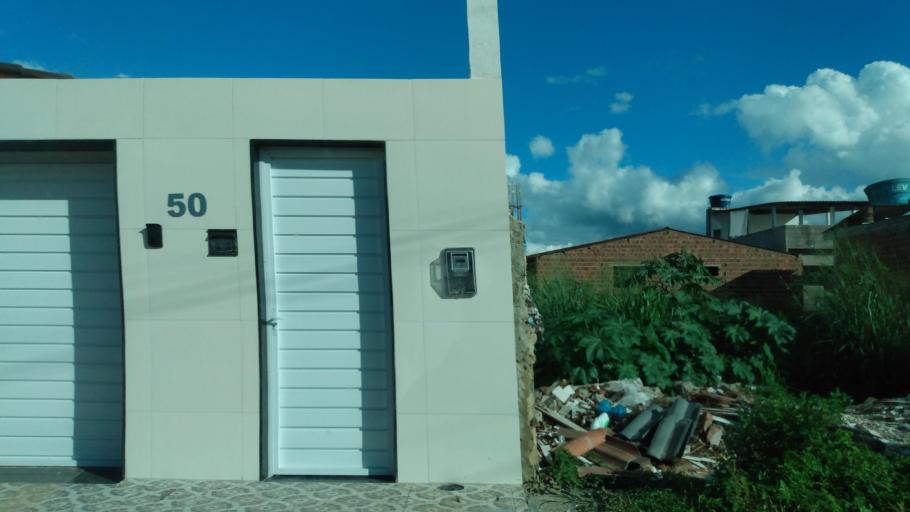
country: BR
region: Pernambuco
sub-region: Gravata
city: Gravata
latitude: -8.1999
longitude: -35.5819
